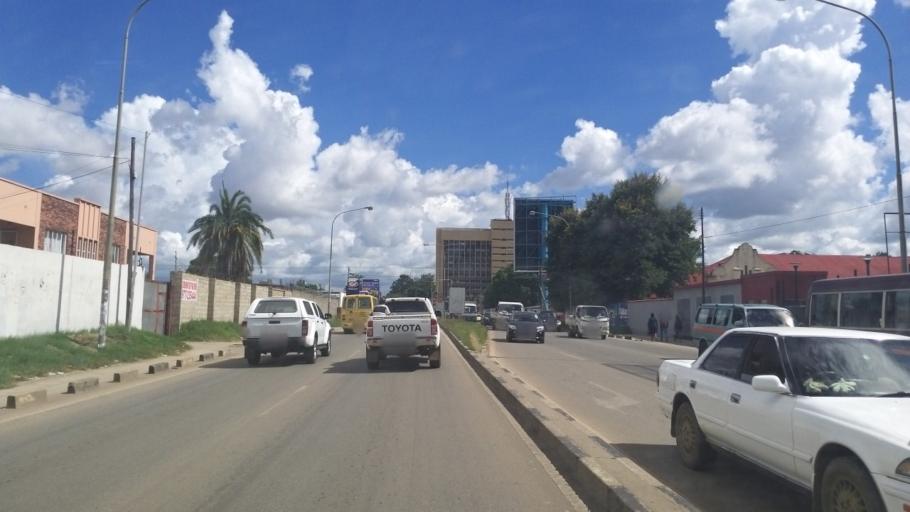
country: ZM
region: Lusaka
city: Lusaka
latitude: -15.4052
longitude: 28.2794
